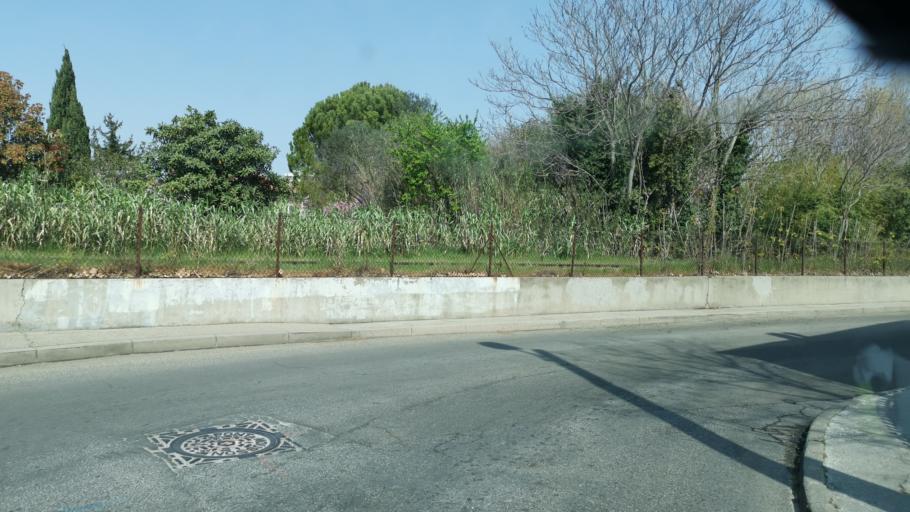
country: FR
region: Provence-Alpes-Cote d'Azur
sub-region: Departement des Bouches-du-Rhone
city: Arles
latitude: 43.6726
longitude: 4.6325
